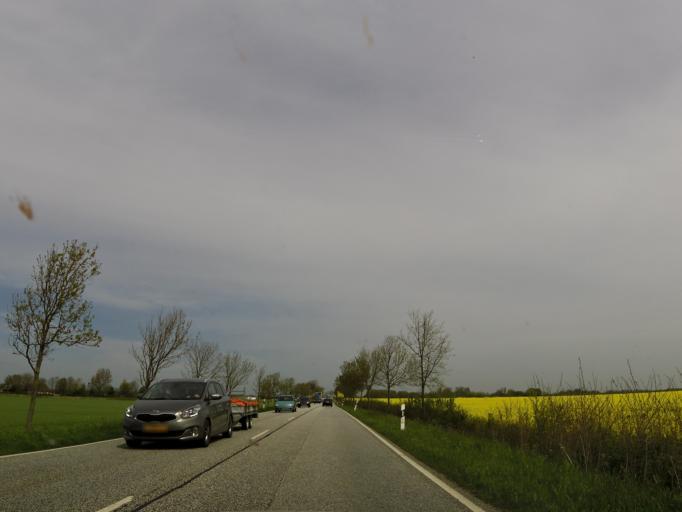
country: DE
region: Schleswig-Holstein
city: Witzwort
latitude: 54.3644
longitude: 8.9768
